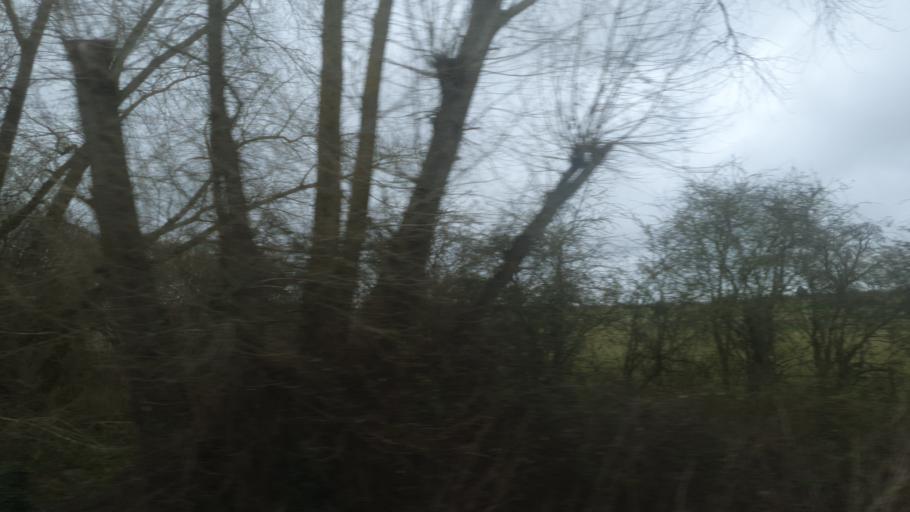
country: GB
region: England
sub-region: West Sussex
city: Pulborough
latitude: 50.9617
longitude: -0.5088
